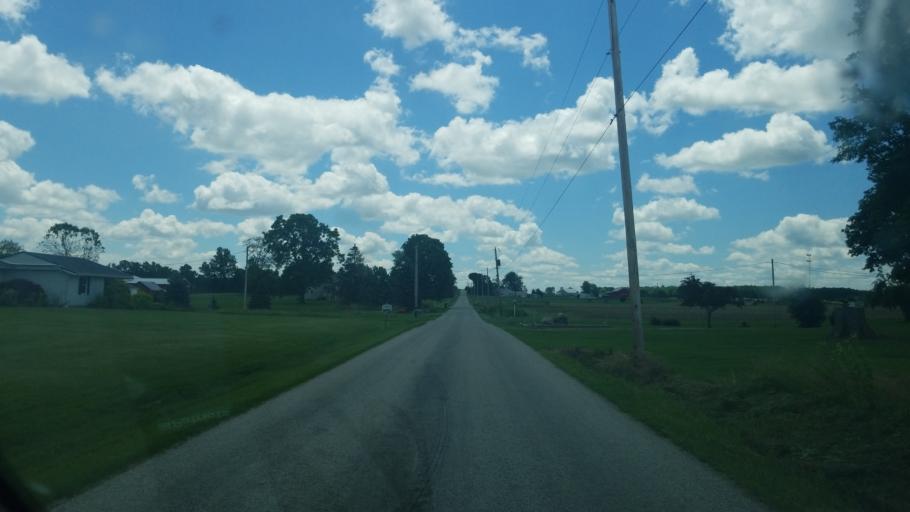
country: US
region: Ohio
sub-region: Huron County
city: New London
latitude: 41.0044
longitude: -82.3255
